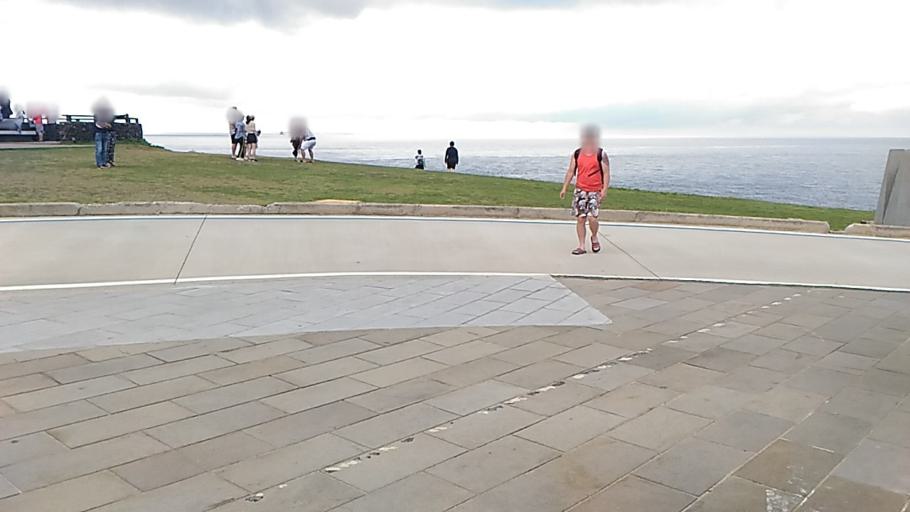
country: TW
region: Taiwan
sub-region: Penghu
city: Ma-kung
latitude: 23.2193
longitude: 119.4463
